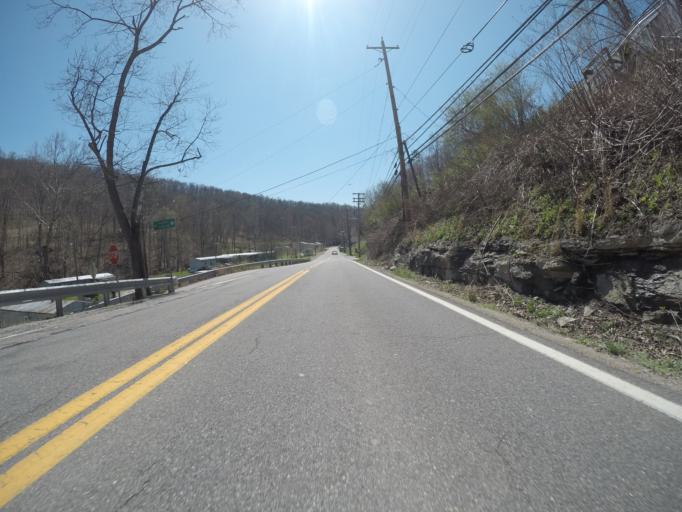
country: US
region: West Virginia
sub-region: Kanawha County
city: Coal Fork
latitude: 38.3819
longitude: -81.5615
